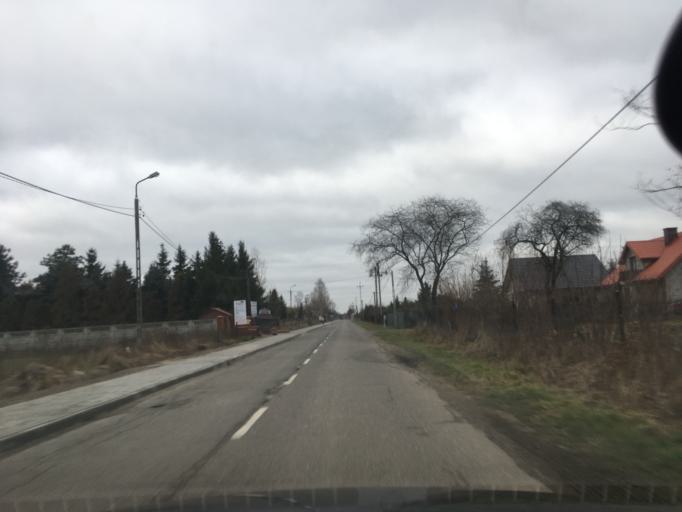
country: PL
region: Masovian Voivodeship
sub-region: Powiat piaseczynski
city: Lesznowola
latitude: 52.0426
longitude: 20.9540
